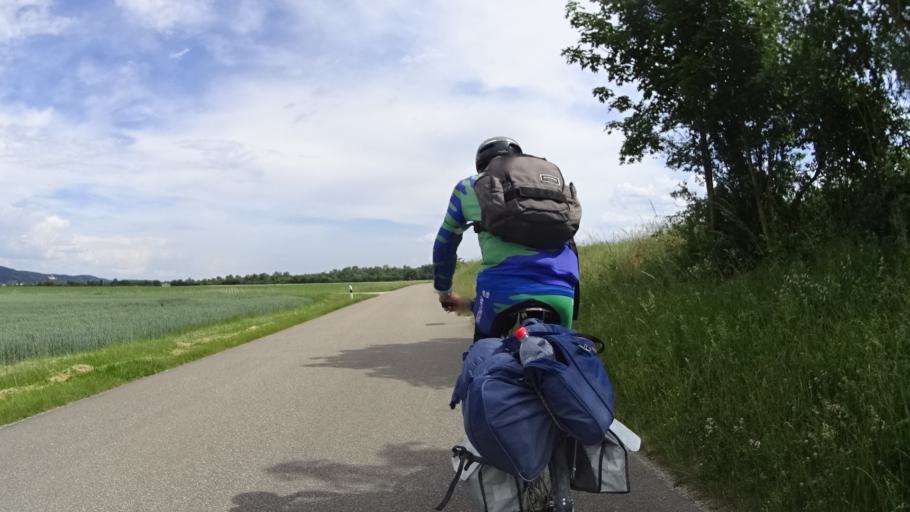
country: DE
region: Bavaria
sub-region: Upper Palatinate
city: Wiesent
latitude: 49.0028
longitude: 12.3413
